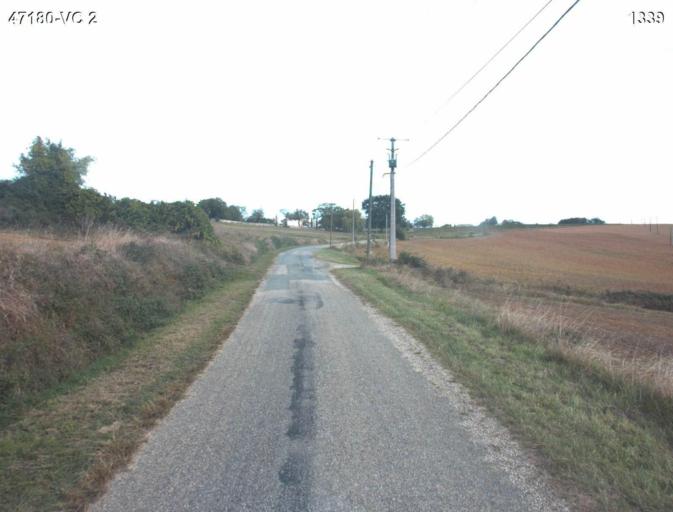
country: FR
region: Aquitaine
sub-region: Departement du Lot-et-Garonne
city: Sainte-Colombe-en-Bruilhois
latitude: 44.1675
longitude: 0.4353
